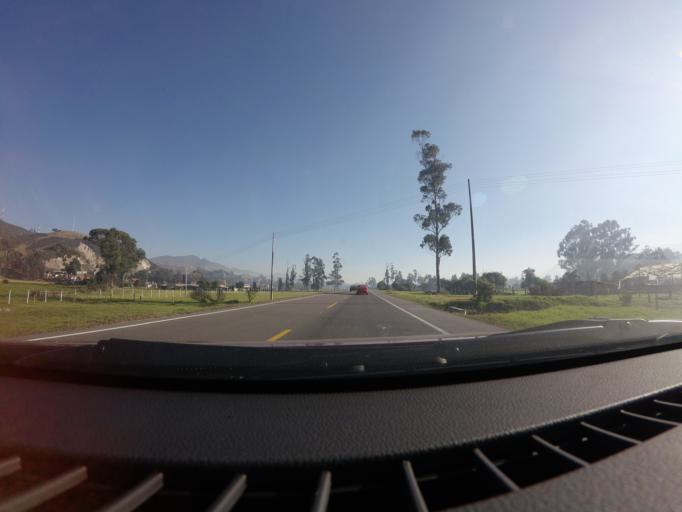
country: CO
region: Cundinamarca
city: Cogua
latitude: 5.0498
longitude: -73.9610
